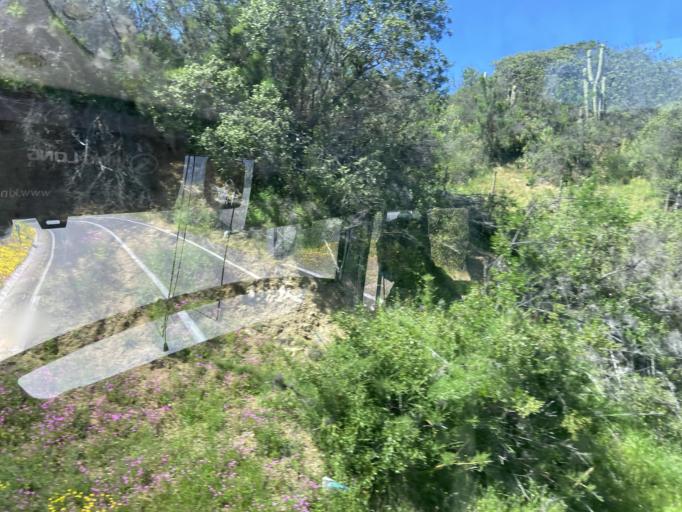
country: CL
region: Valparaiso
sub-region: Provincia de Marga Marga
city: Villa Alemana
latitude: -33.1921
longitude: -71.2858
